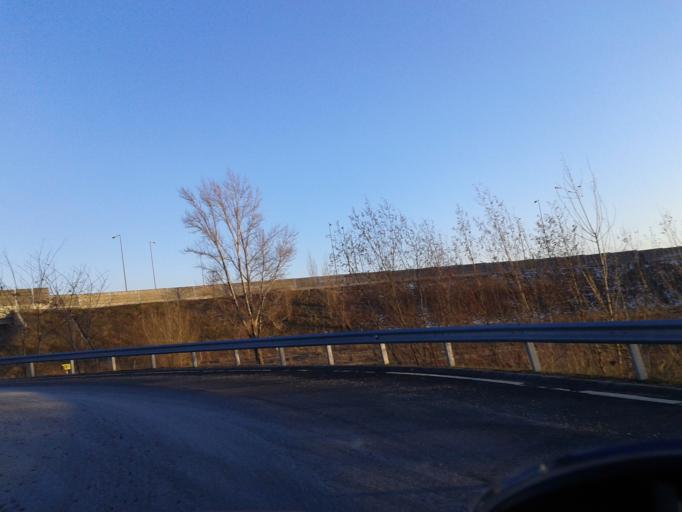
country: HU
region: Pest
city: Diosd
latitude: 47.4011
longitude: 18.9725
